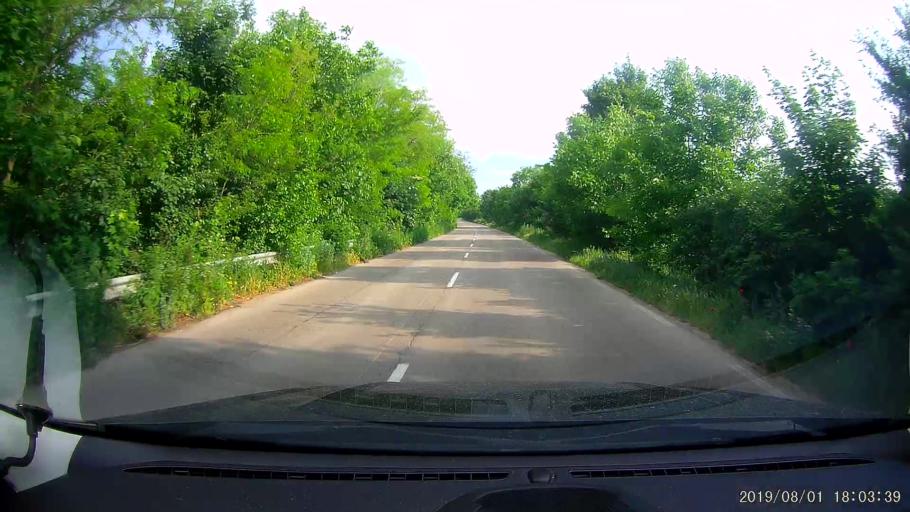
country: BG
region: Silistra
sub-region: Obshtina Alfatar
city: Alfatar
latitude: 43.9227
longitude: 27.2890
